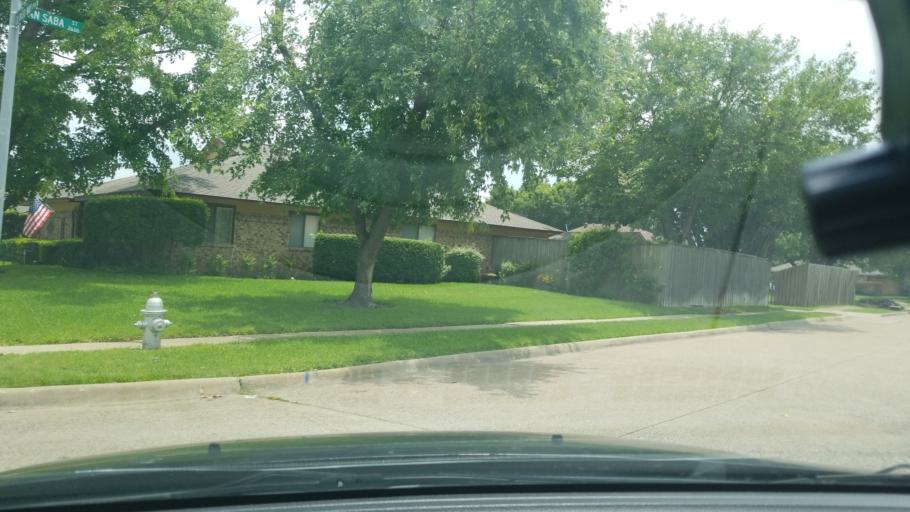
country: US
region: Texas
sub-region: Dallas County
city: Mesquite
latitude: 32.8005
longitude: -96.6201
